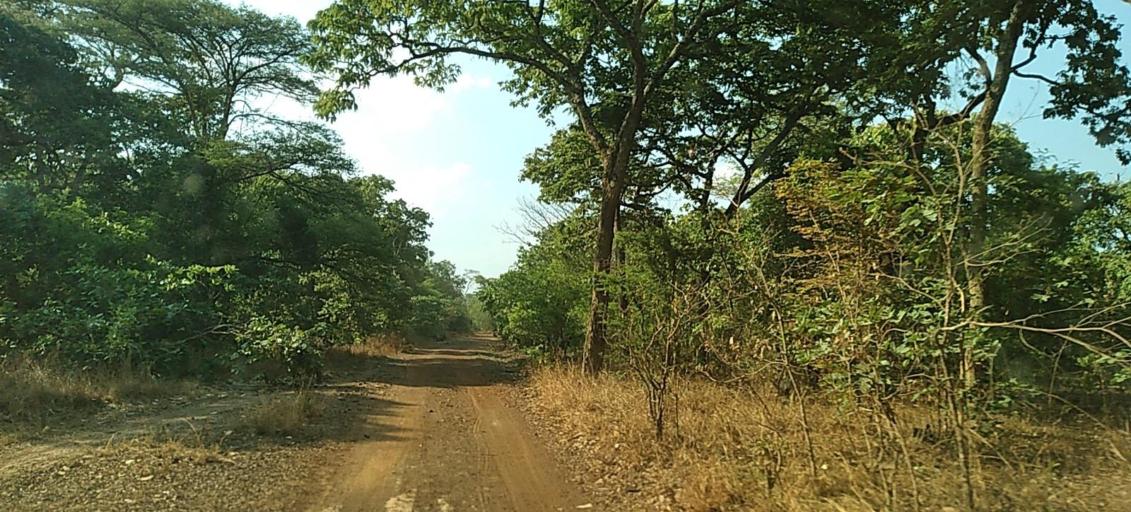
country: ZM
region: Copperbelt
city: Mpongwe
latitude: -13.4506
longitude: 28.0654
